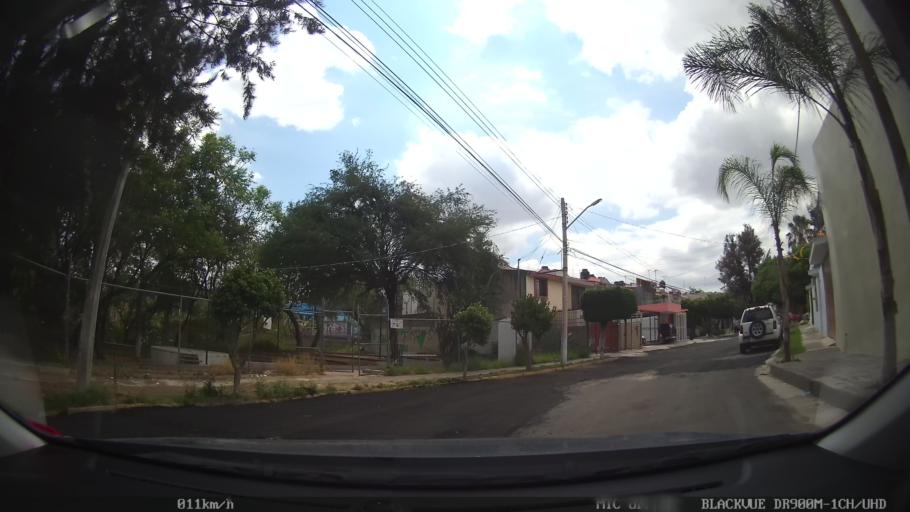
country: MX
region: Jalisco
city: Tonala
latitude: 20.6282
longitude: -103.2515
